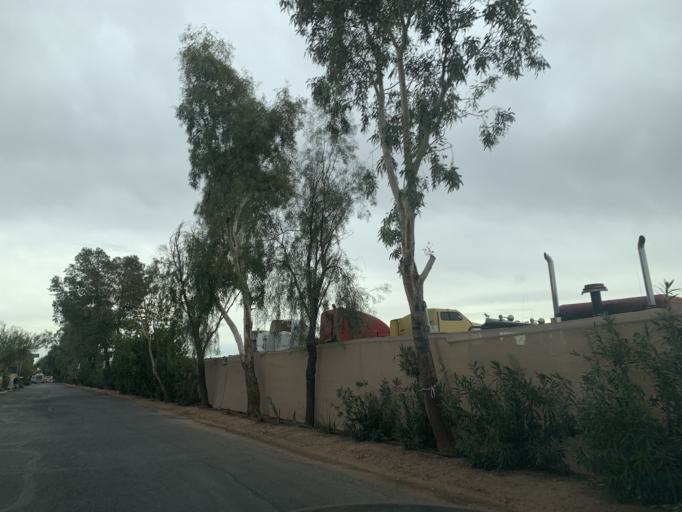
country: US
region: Arizona
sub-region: Pinal County
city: Arizona City
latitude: 32.8141
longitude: -111.6756
